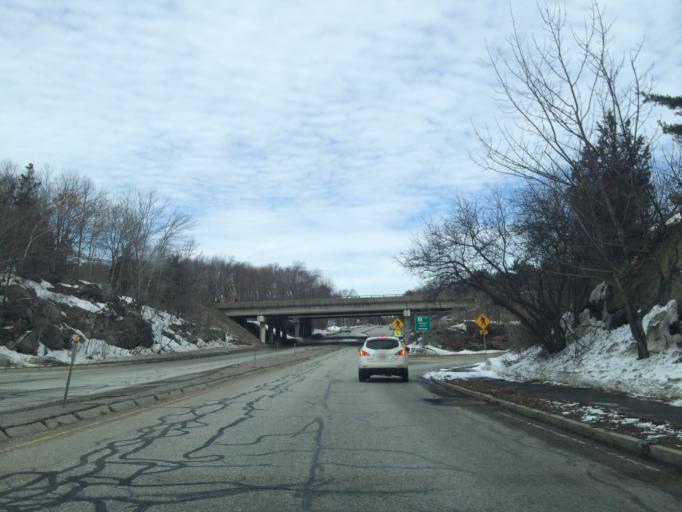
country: US
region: Massachusetts
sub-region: Middlesex County
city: Lexington
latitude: 42.4205
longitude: -71.2318
